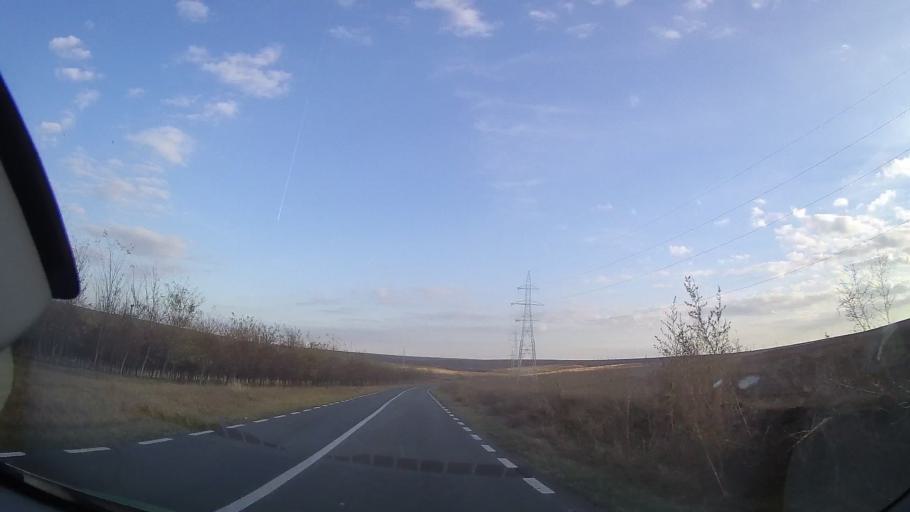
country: RO
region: Constanta
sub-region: Comuna Chirnogeni
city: Plopeni
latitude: 43.9573
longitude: 28.1478
